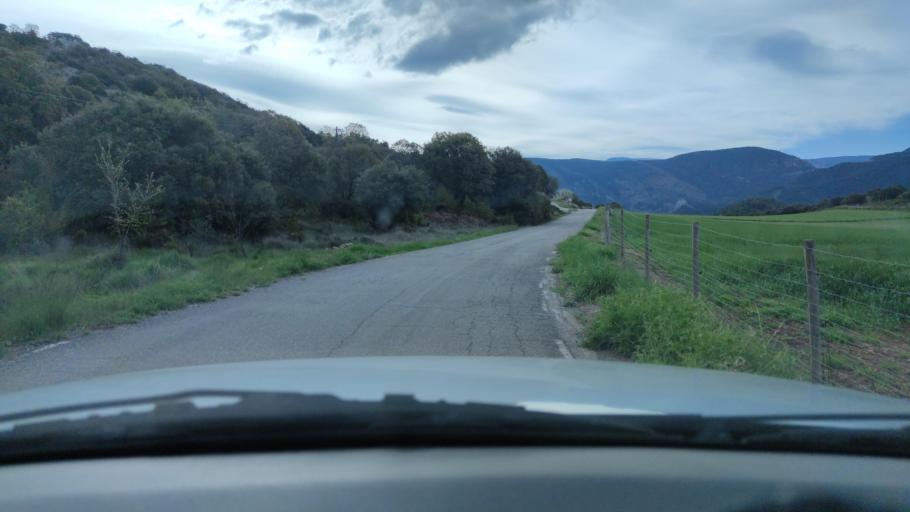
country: ES
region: Catalonia
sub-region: Provincia de Lleida
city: Coll de Nargo
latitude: 42.2395
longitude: 1.3786
